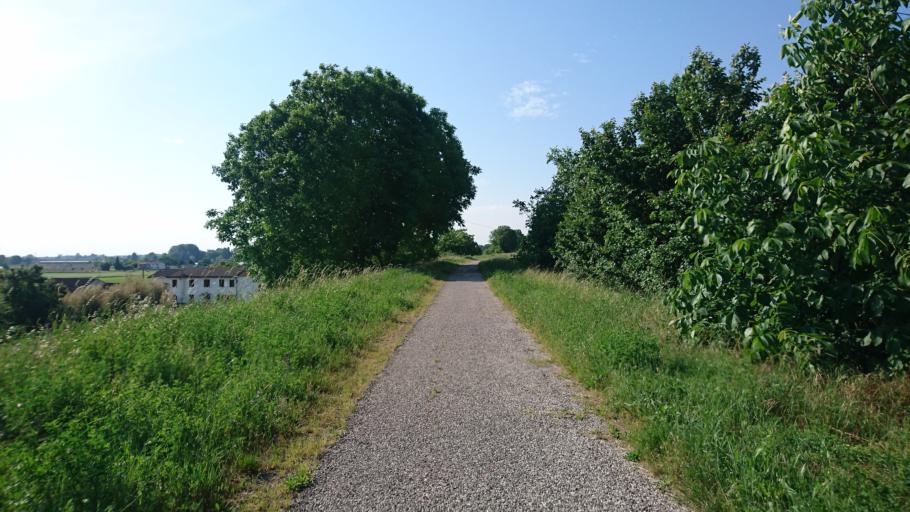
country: IT
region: Veneto
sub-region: Provincia di Verona
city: Villa Bartolomea
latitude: 45.1830
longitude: 11.3280
